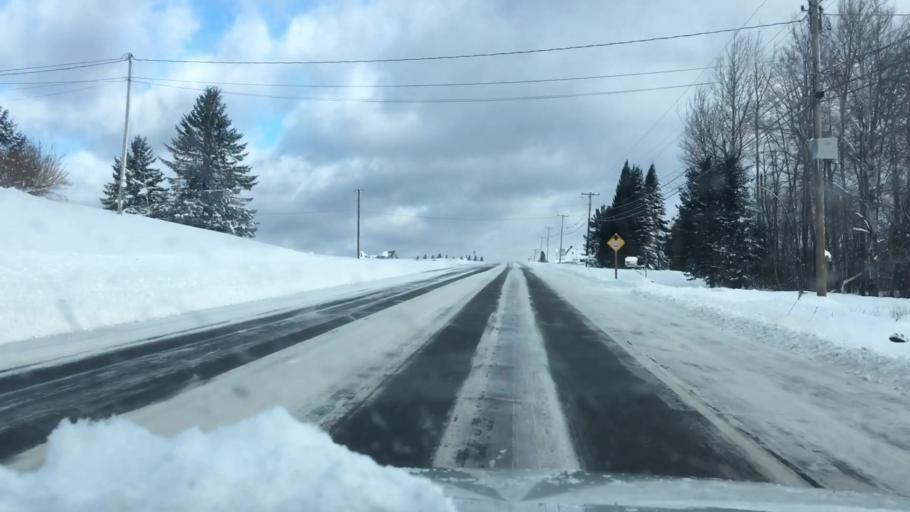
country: US
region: Maine
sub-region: Aroostook County
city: Caribou
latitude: 46.9343
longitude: -68.0233
